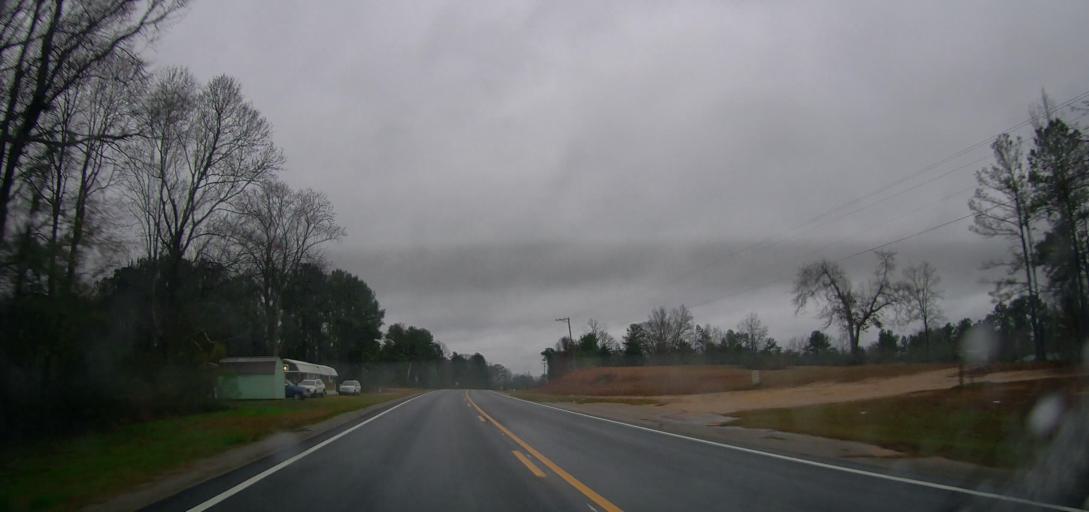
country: US
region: Alabama
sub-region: Chilton County
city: Thorsby
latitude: 32.7996
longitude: -86.9118
